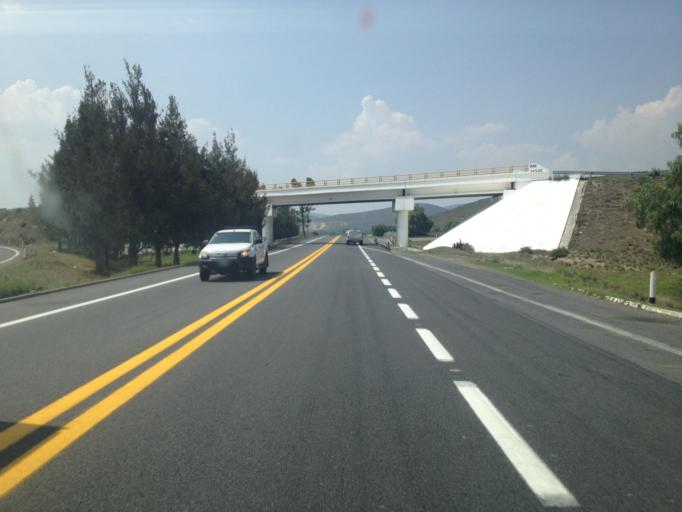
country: MX
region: Puebla
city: Cuacnopalan
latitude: 18.8130
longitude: -97.4908
